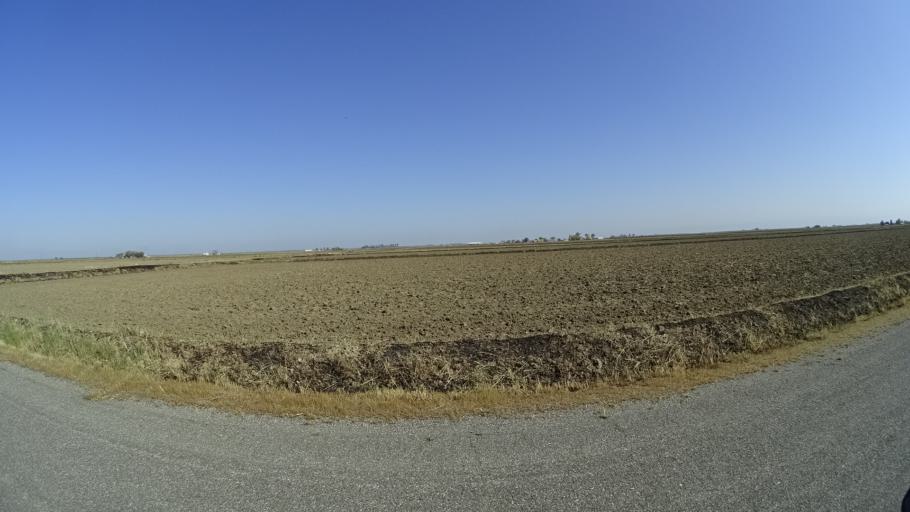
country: US
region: California
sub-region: Glenn County
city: Willows
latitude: 39.6016
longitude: -122.0693
